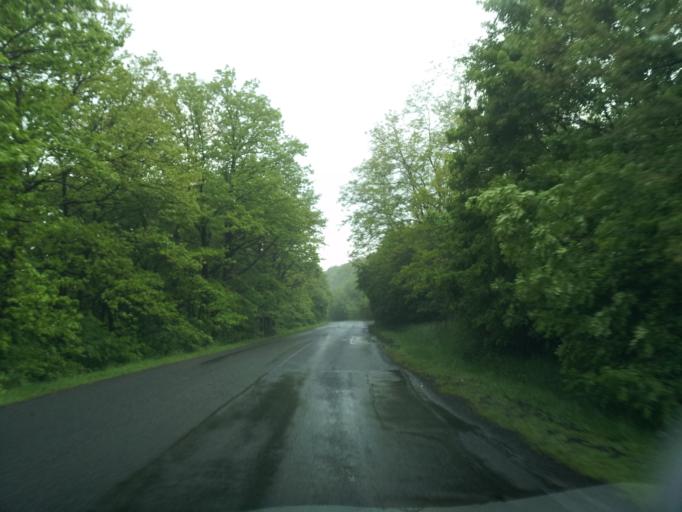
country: HU
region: Baranya
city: Hosszuheteny
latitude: 46.1691
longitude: 18.3371
